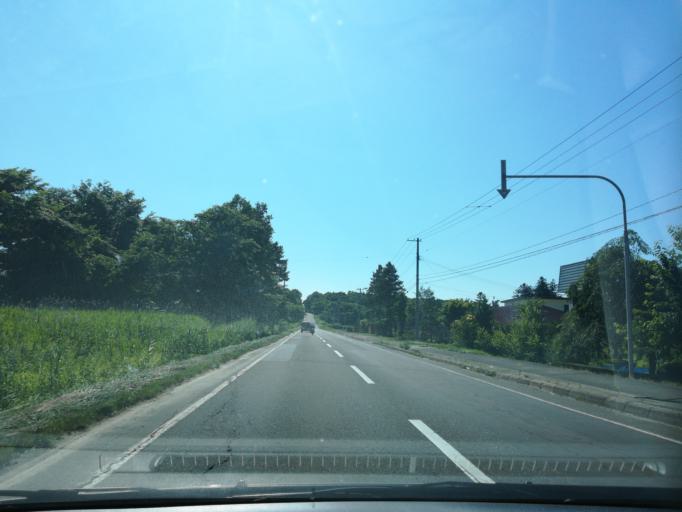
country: JP
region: Hokkaido
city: Chitose
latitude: 42.9146
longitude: 141.8866
